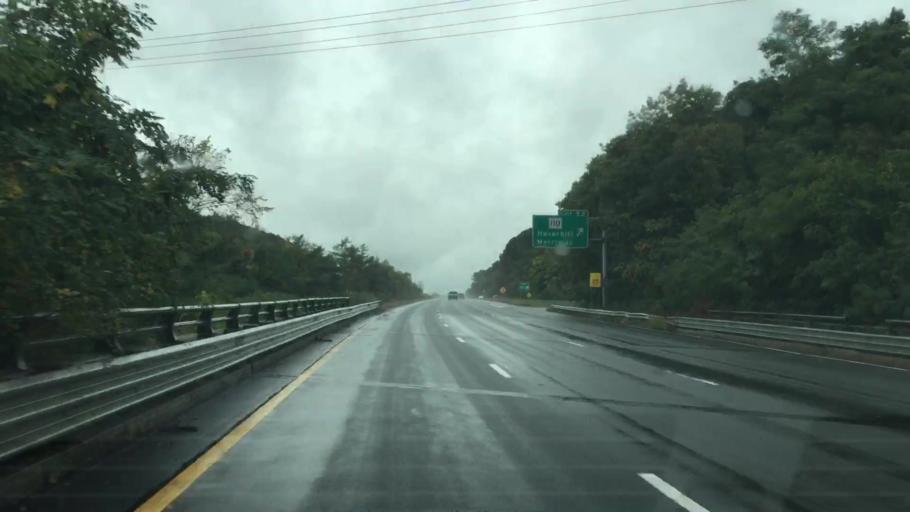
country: US
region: Massachusetts
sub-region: Essex County
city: Haverhill
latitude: 42.8026
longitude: -71.0515
